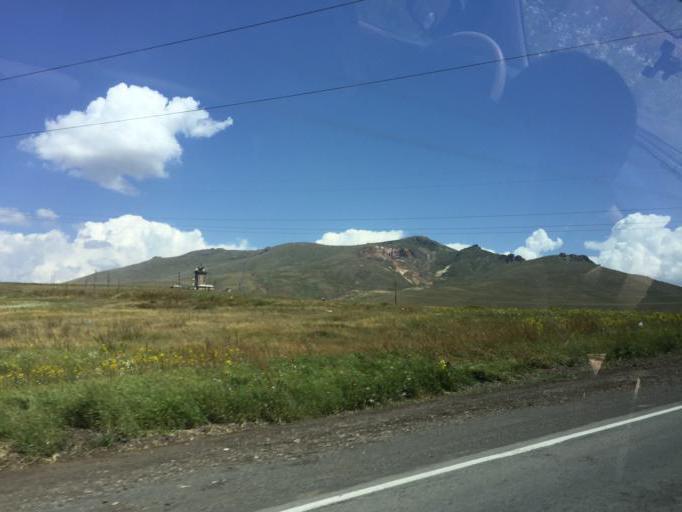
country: AM
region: Vayots' Dzori Marz
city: Jermuk
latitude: 39.6865
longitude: 45.7121
